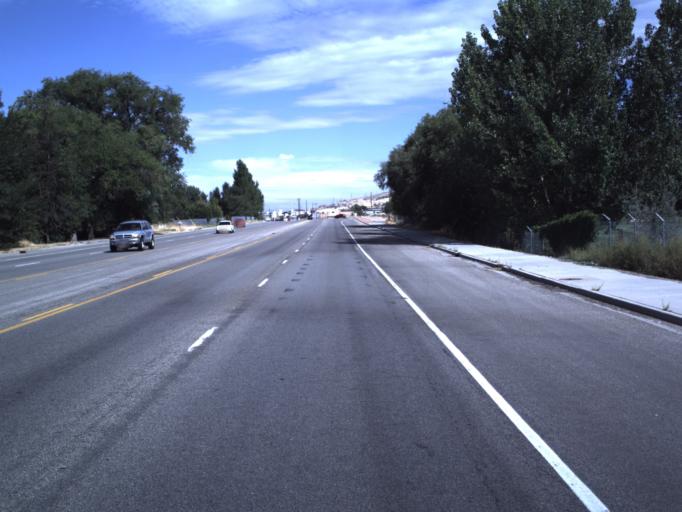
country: US
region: Utah
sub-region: Weber County
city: Harrisville
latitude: 41.2920
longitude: -111.9927
